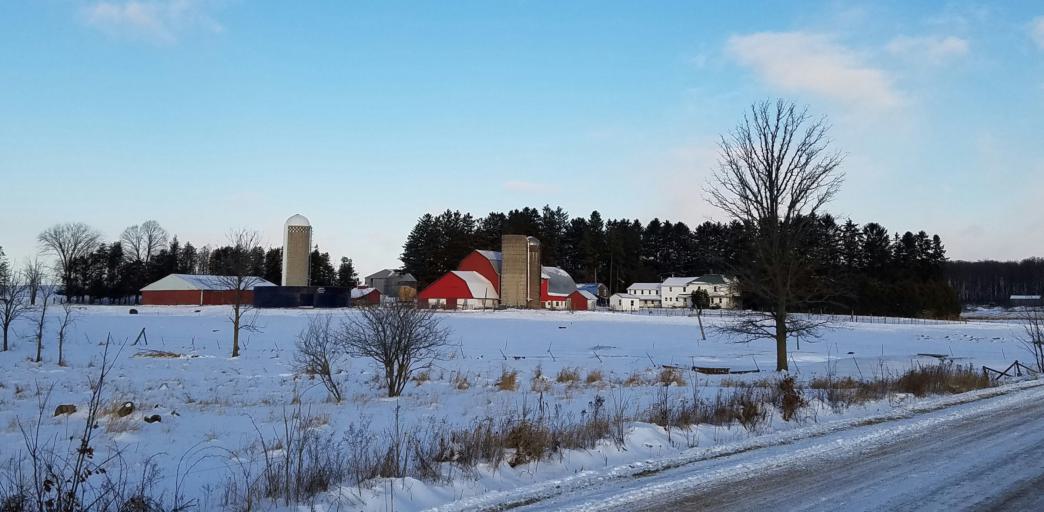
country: US
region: Wisconsin
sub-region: Clark County
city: Loyal
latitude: 44.6358
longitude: -90.4563
